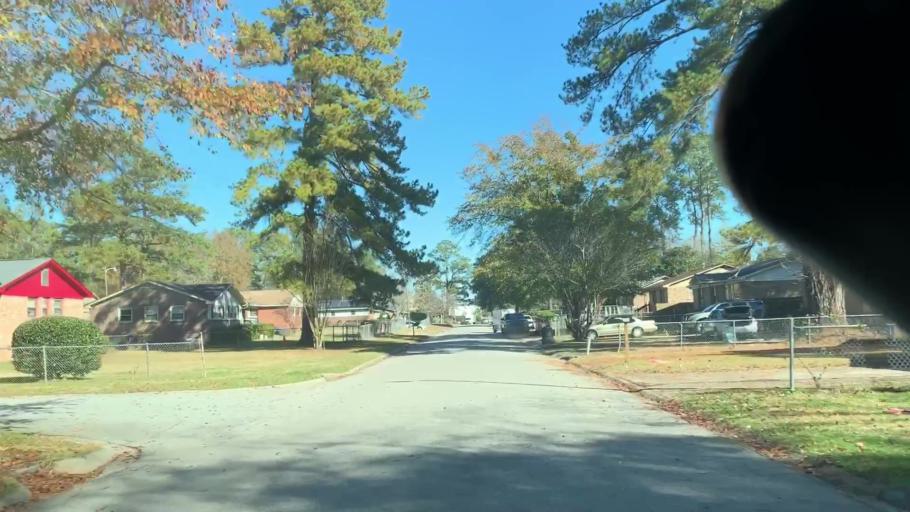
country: US
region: South Carolina
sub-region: Richland County
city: Forest Acres
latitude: 33.9352
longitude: -80.9655
